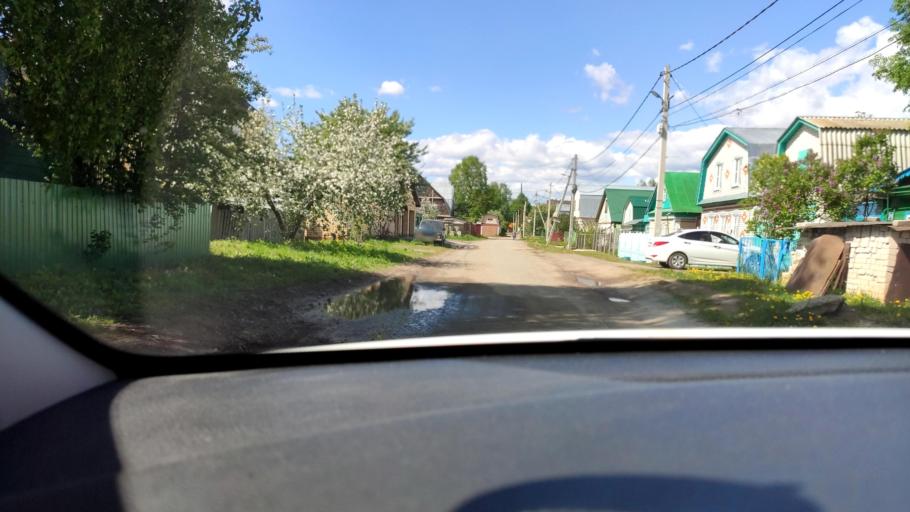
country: RU
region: Tatarstan
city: Stolbishchi
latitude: 55.7037
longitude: 49.1504
